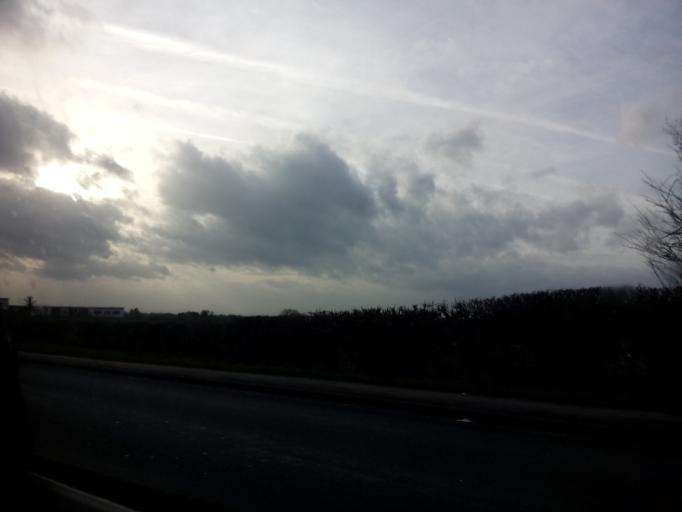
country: GB
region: England
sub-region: Worcestershire
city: Bromsgrove
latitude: 52.3605
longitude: -2.0462
